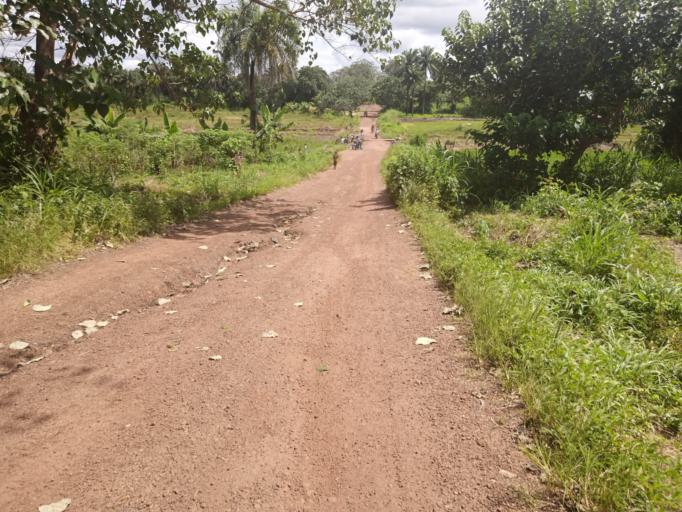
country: SL
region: Northern Province
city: Kamakwie
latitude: 9.4913
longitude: -12.2455
